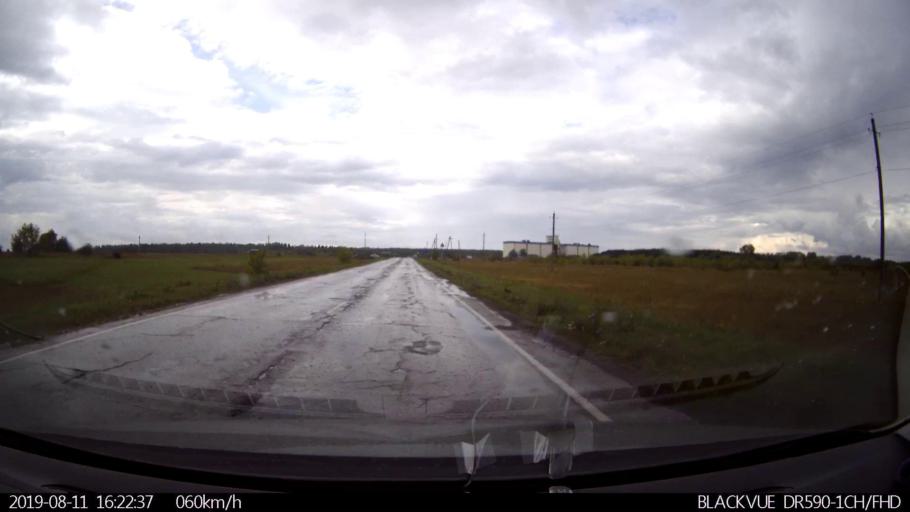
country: RU
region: Ulyanovsk
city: Mayna
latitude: 54.0895
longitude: 47.5920
